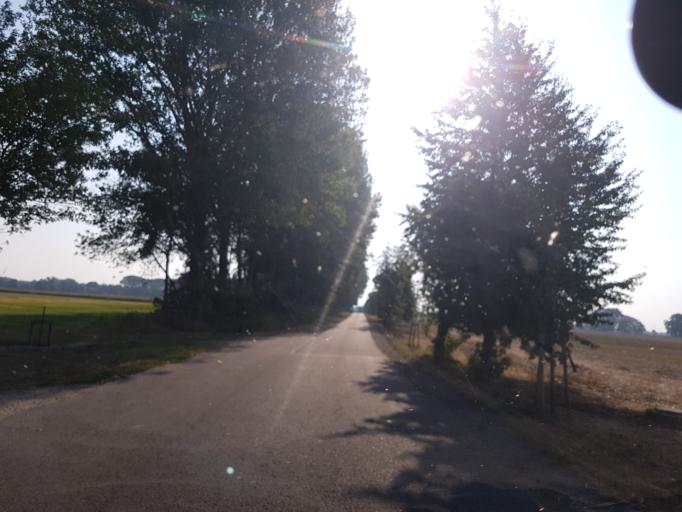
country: DE
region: Brandenburg
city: Finsterwalde
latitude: 51.6868
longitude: 13.7021
